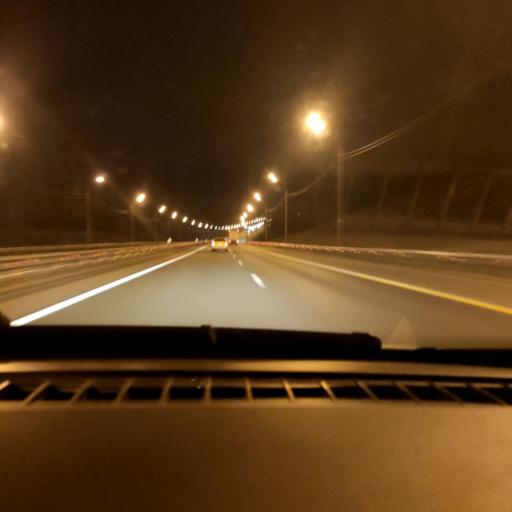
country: RU
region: Lipetsk
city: Khlevnoye
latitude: 52.2228
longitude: 39.1132
